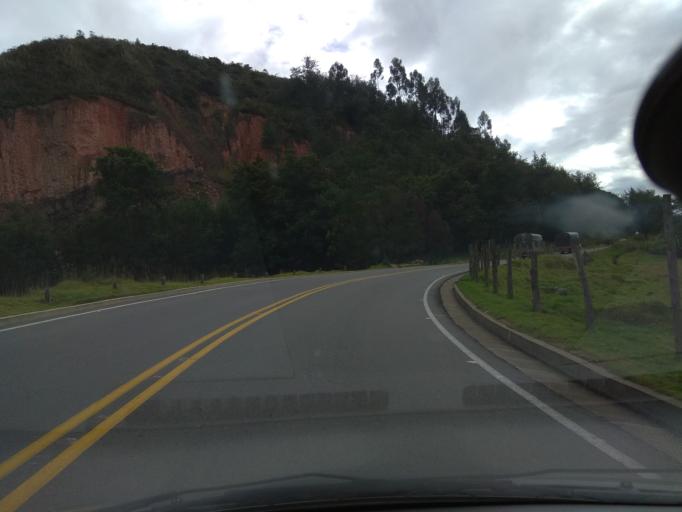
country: CO
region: Boyaca
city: Santa Rosa de Viterbo
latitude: 5.8650
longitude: -73.0062
